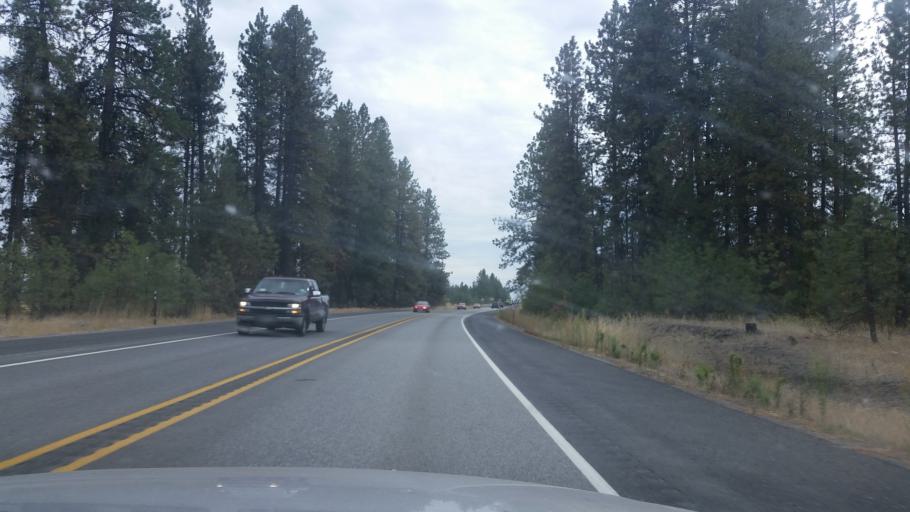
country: US
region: Washington
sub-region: Spokane County
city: Cheney
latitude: 47.5182
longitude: -117.5648
